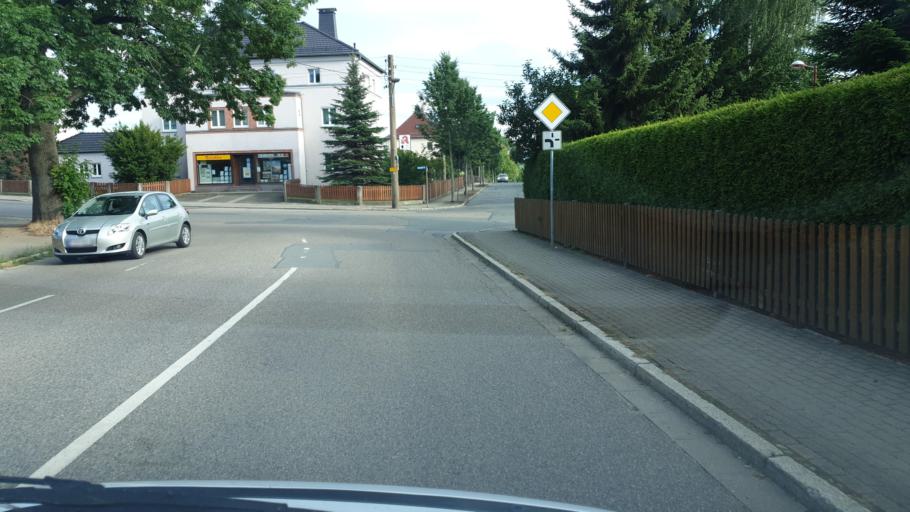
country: DE
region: Saxony
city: Hohenstein-Ernstthal
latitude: 50.8015
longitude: 12.7285
